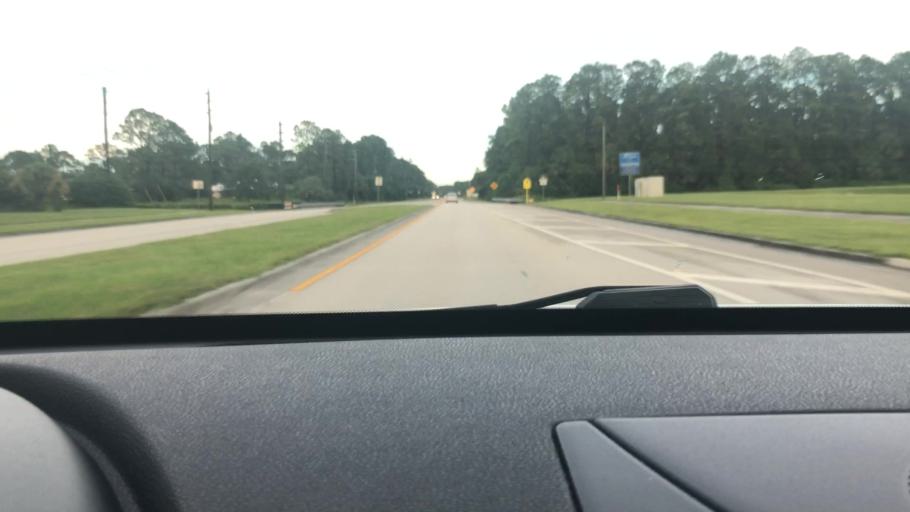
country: US
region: Florida
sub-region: Sarasota County
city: North Port
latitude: 27.0684
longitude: -82.1535
